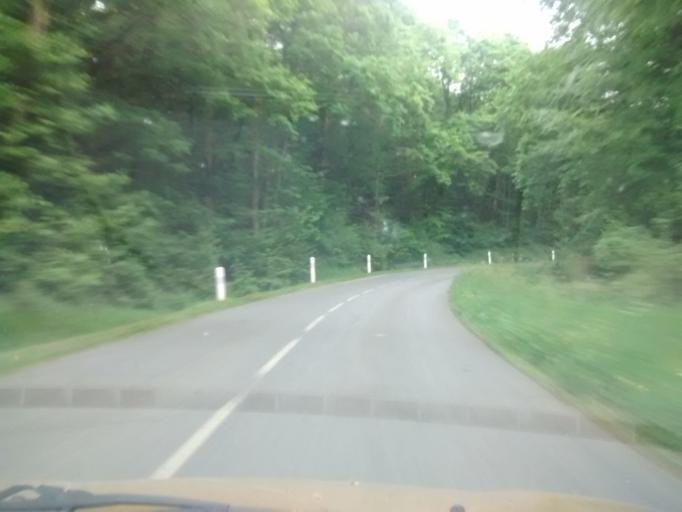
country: FR
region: Brittany
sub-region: Departement du Morbihan
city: Pluherlin
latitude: 47.7228
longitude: -2.3416
